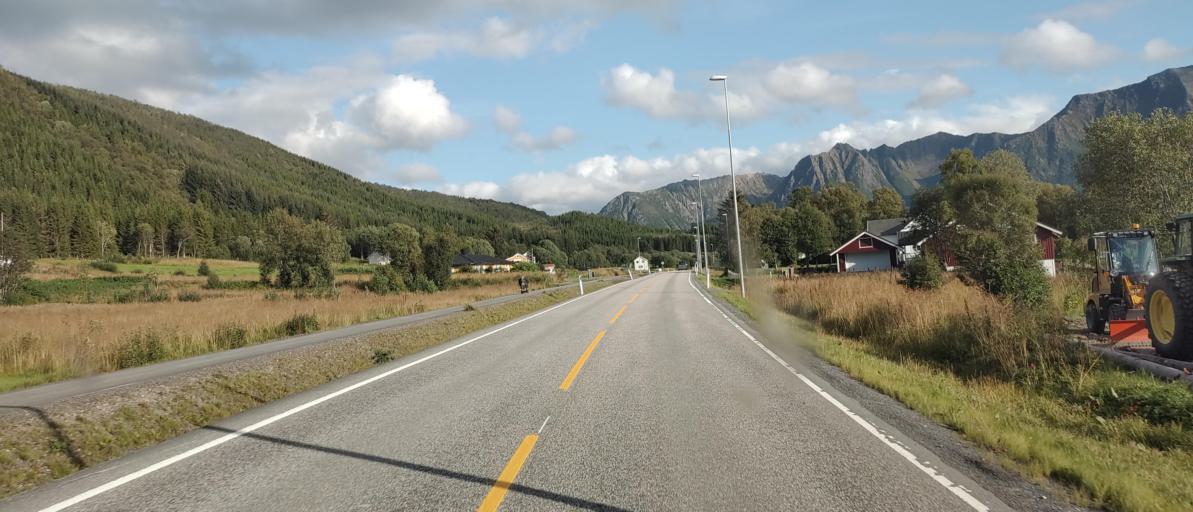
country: NO
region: Nordland
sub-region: Sortland
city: Sortland
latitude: 68.7505
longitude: 15.4906
